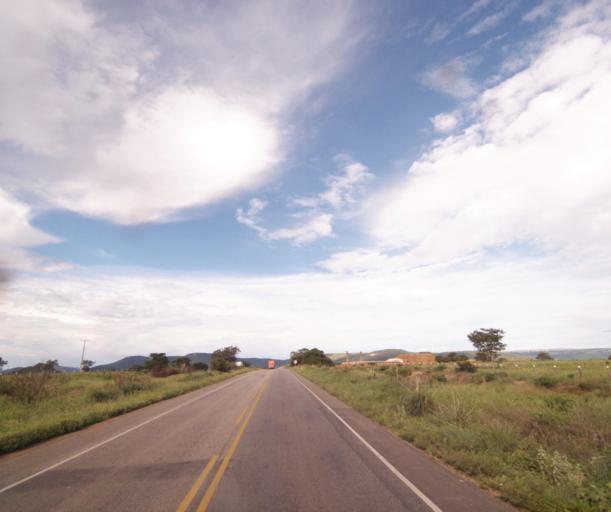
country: BR
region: Bahia
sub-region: Guanambi
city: Guanambi
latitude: -14.1940
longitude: -42.7474
